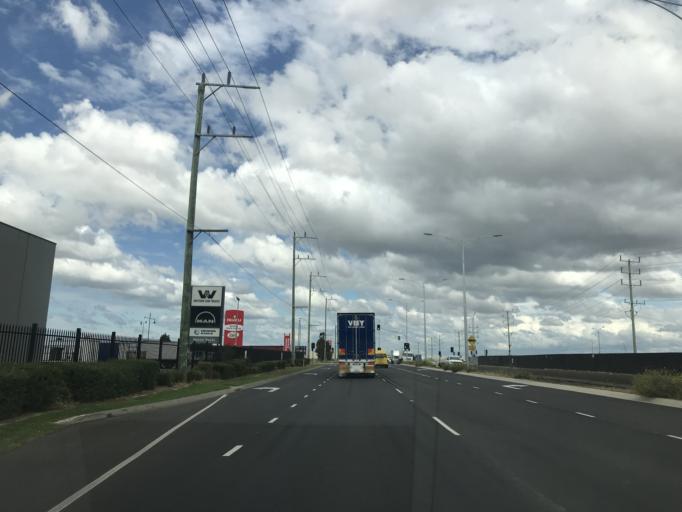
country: AU
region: Victoria
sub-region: Wyndham
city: Truganina
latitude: -37.8018
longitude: 144.7521
